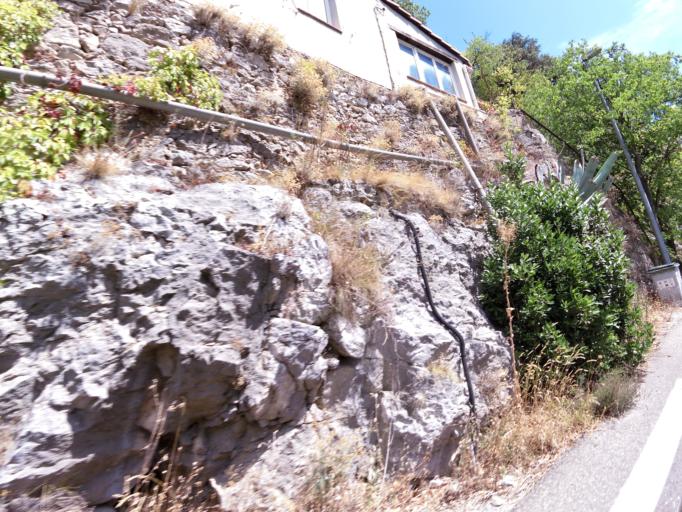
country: FR
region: Languedoc-Roussillon
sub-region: Departement de l'Herault
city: Ganges
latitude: 43.9375
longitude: 3.6950
